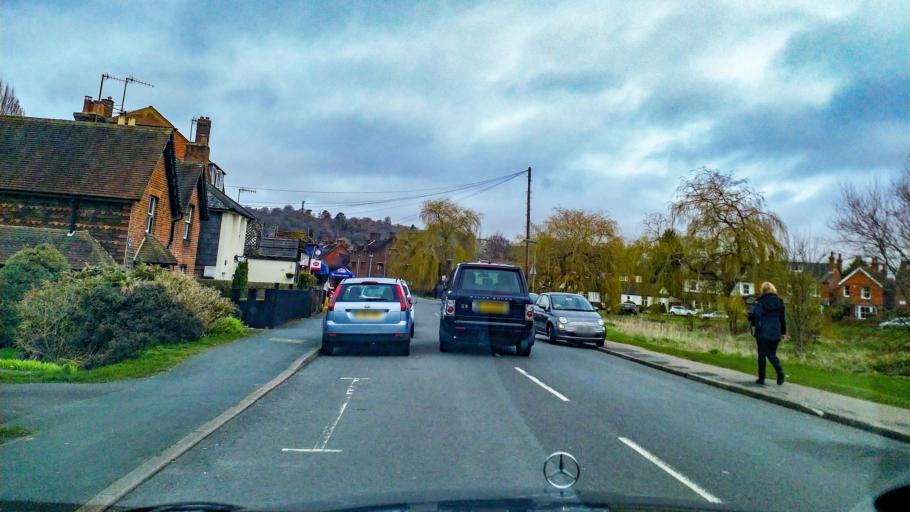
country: GB
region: England
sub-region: Surrey
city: Dorking
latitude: 51.2130
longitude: -0.3285
